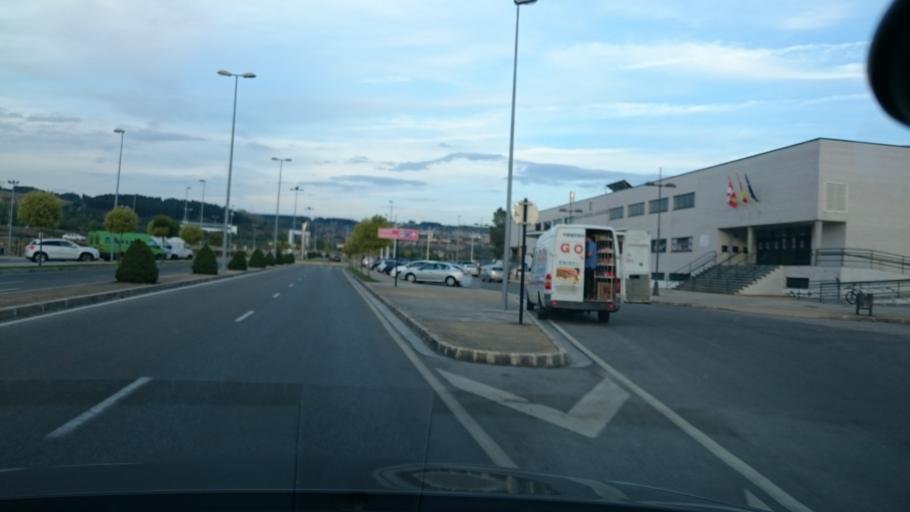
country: ES
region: Castille and Leon
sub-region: Provincia de Leon
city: Ponferrada
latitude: 42.5562
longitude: -6.5998
